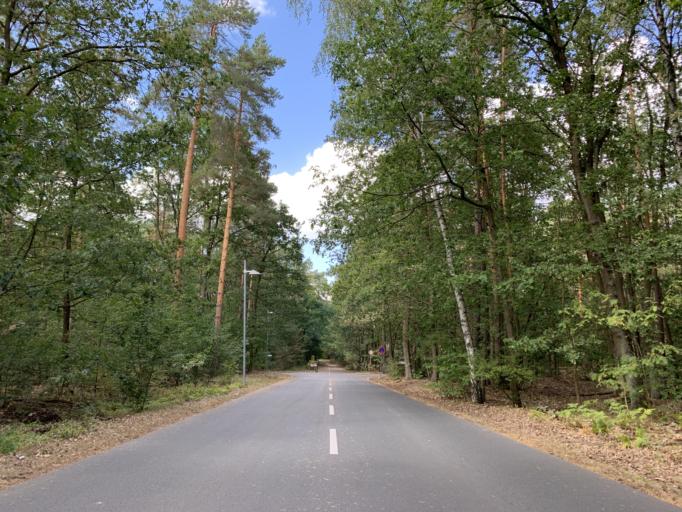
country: DE
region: Berlin
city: Wannsee
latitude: 52.4067
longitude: 13.1826
